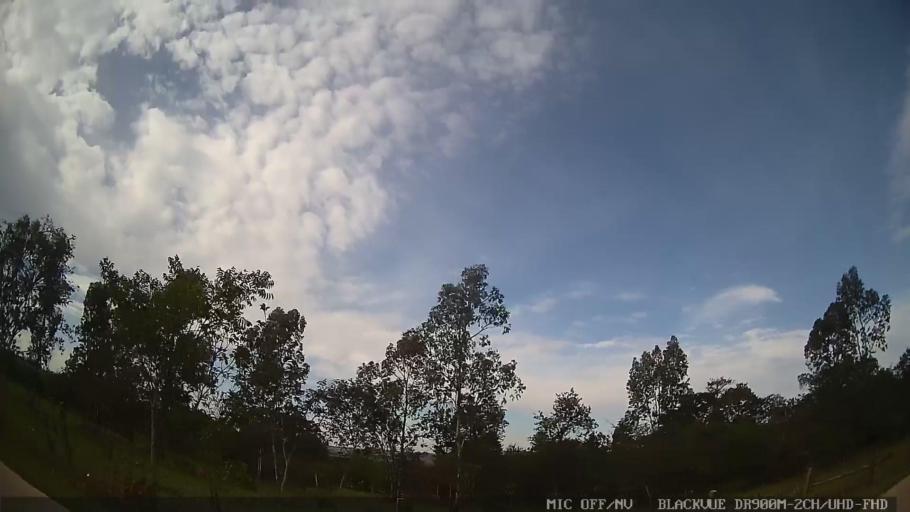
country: BR
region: Sao Paulo
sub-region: Salto
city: Salto
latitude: -23.1759
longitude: -47.2653
